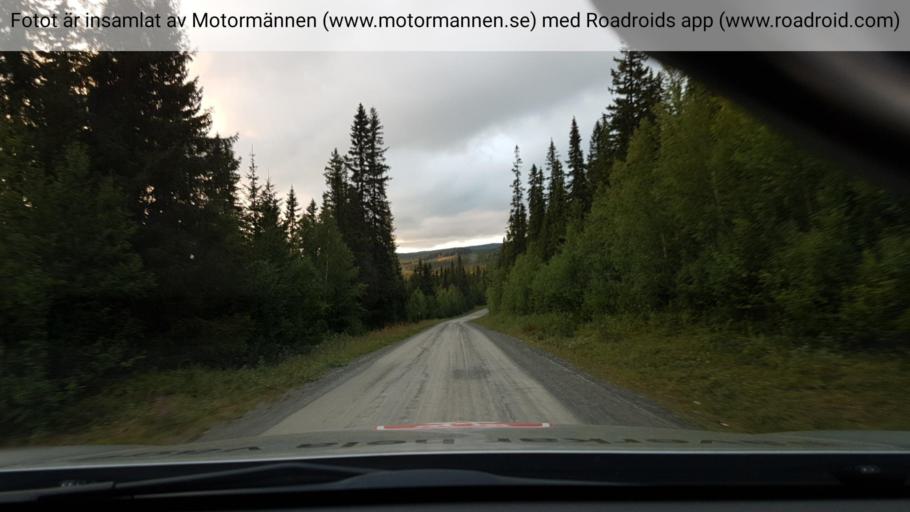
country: SE
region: Vaesterbotten
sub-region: Vilhelmina Kommun
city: Sjoberg
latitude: 65.5468
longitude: 15.4182
